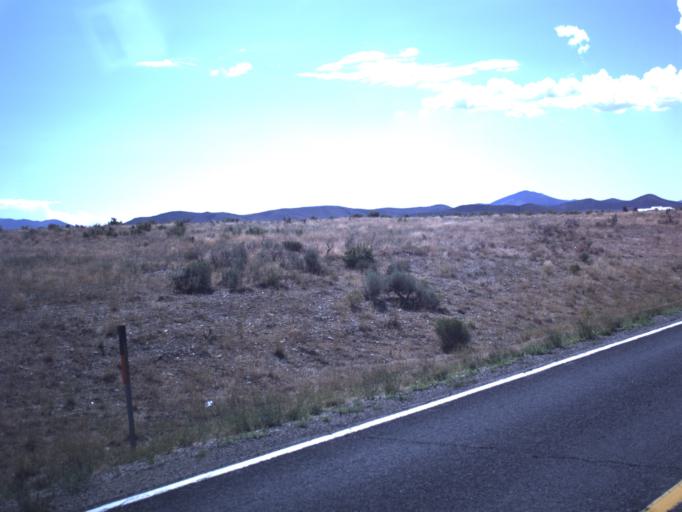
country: US
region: Utah
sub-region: Tooele County
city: Tooele
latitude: 40.1082
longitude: -112.4308
